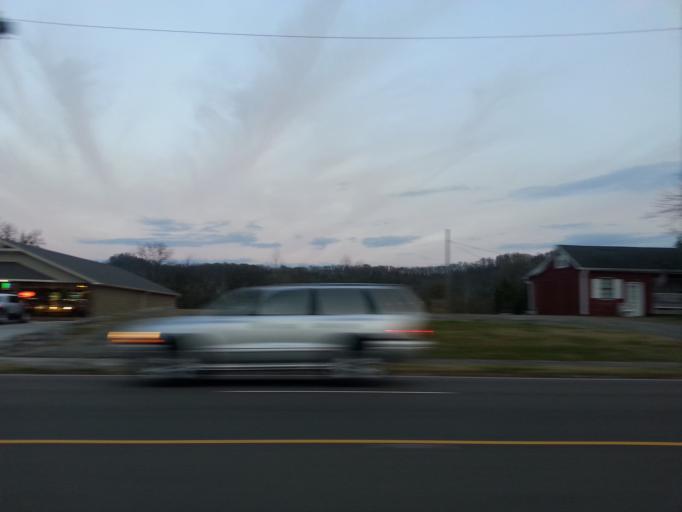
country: US
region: Tennessee
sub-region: McMinn County
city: Etowah
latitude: 35.3388
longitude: -84.5203
